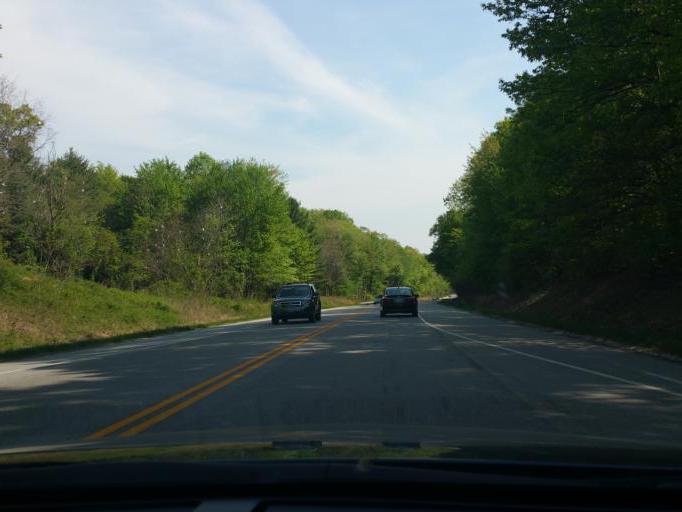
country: US
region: Maryland
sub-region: Cecil County
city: Perryville
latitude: 39.6082
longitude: -76.0684
